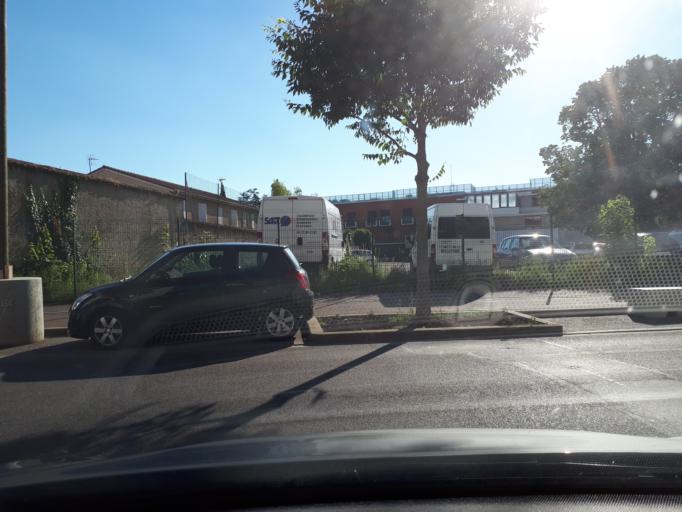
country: FR
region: Rhone-Alpes
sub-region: Departement du Rhone
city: Meyzieu
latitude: 45.7707
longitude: 5.0013
